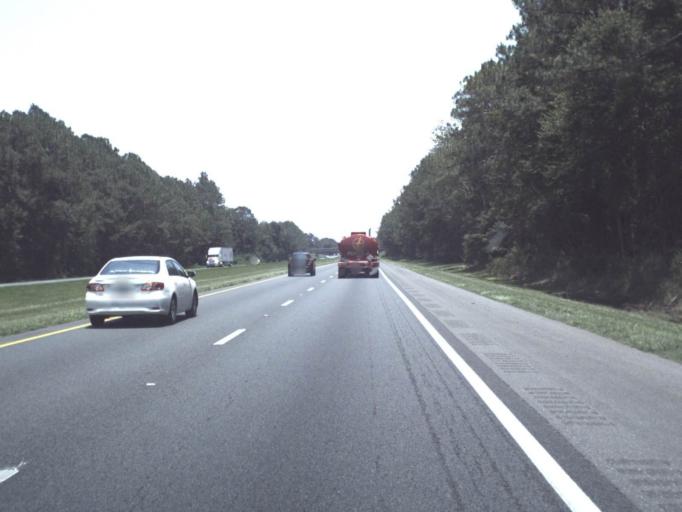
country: US
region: Florida
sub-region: Baker County
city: Macclenny
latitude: 30.2544
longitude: -82.1988
